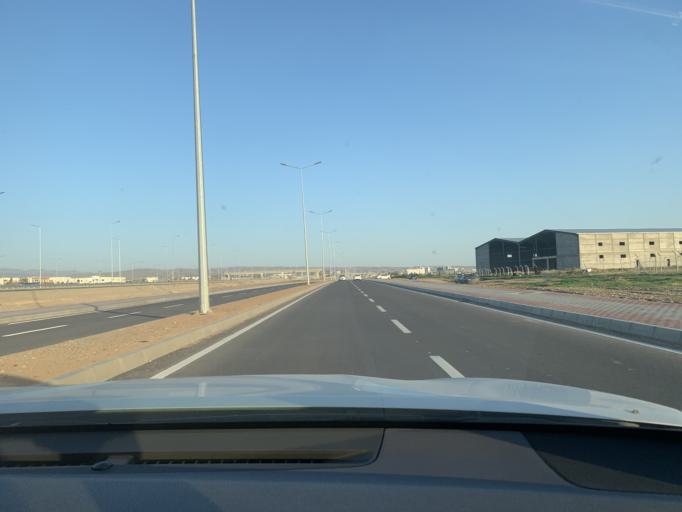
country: IQ
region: Arbil
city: Erbil
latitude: 36.2842
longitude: 44.0515
